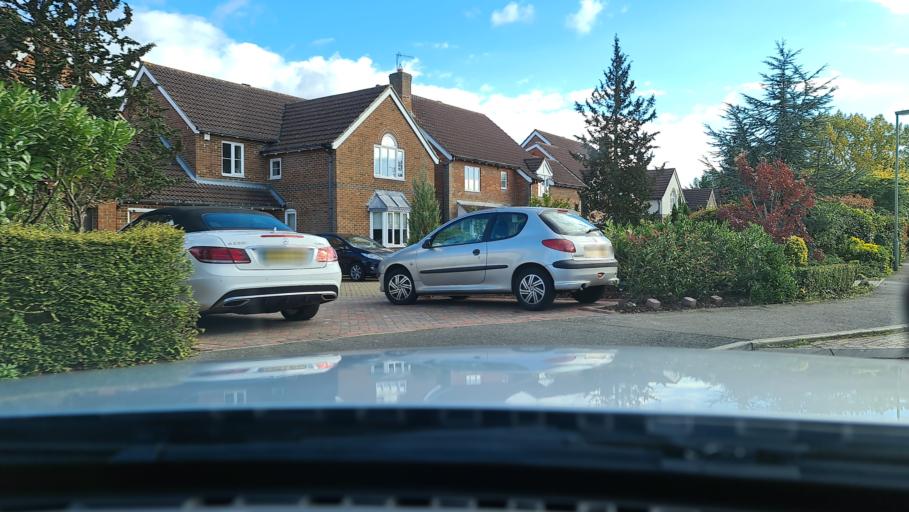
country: GB
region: England
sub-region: Surrey
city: Byfleet
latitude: 51.3475
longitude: -0.4653
